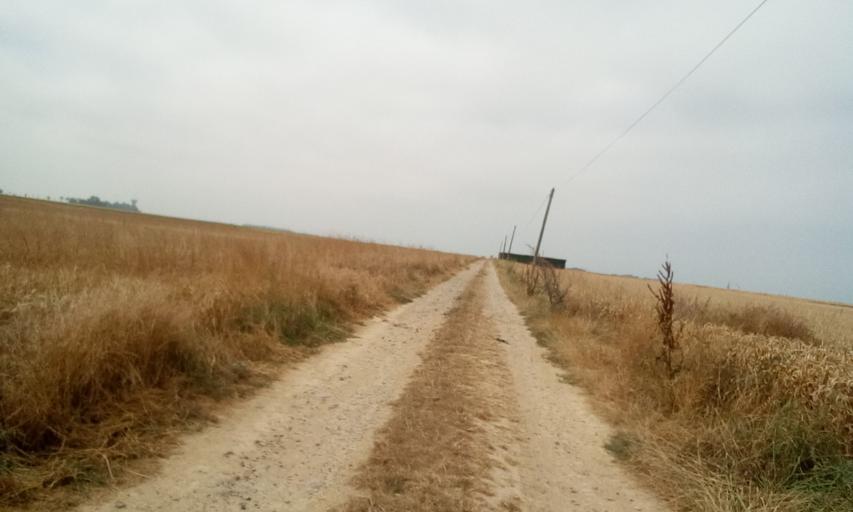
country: FR
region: Lower Normandy
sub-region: Departement du Calvados
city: Douvres-la-Delivrande
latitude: 49.3032
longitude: -0.3782
